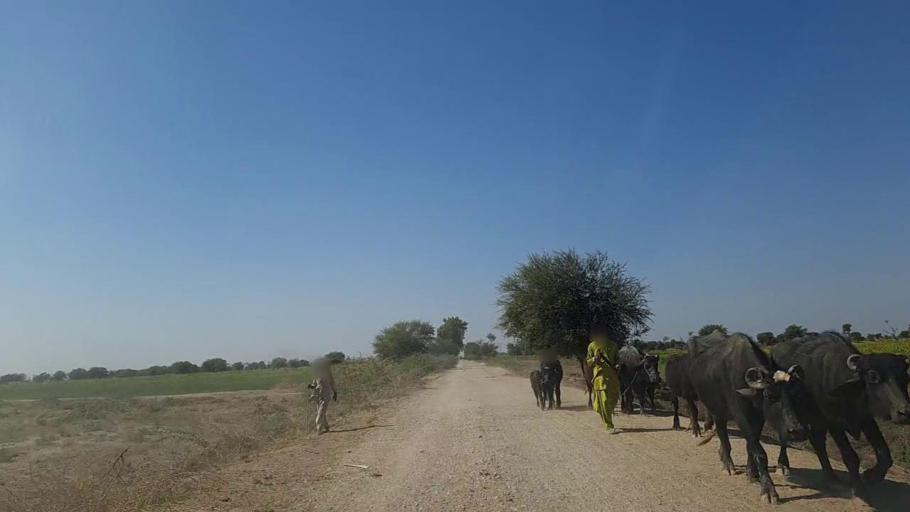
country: PK
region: Sindh
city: Naukot
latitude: 25.0388
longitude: 69.3848
